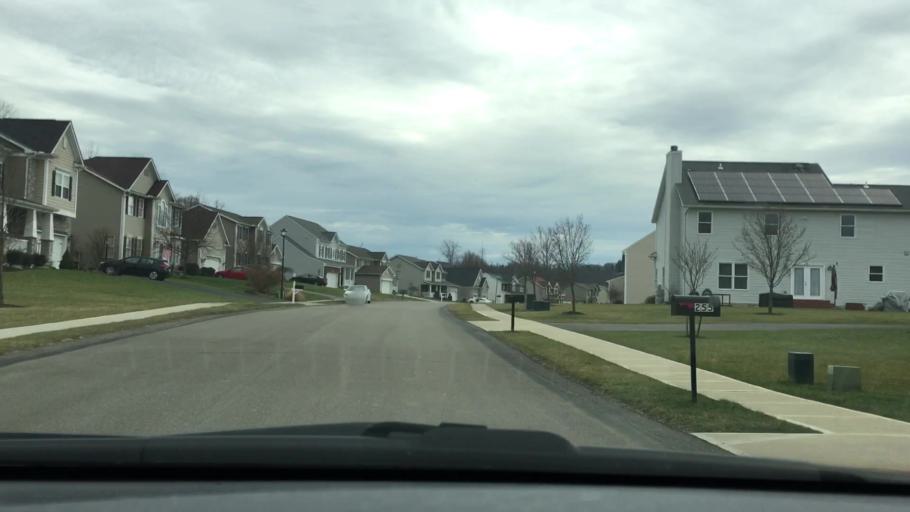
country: US
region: Pennsylvania
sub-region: Allegheny County
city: Sturgeon
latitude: 40.3936
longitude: -80.2095
